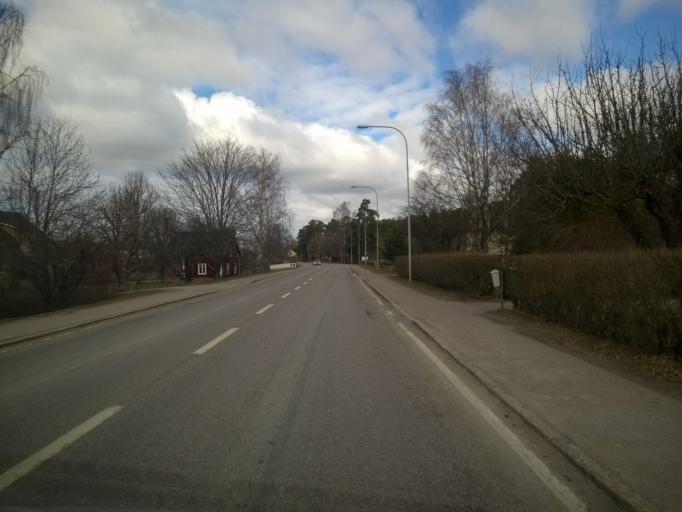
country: SE
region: Uppsala
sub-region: Tierps Kommun
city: Tierp
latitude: 60.2241
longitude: 17.4672
